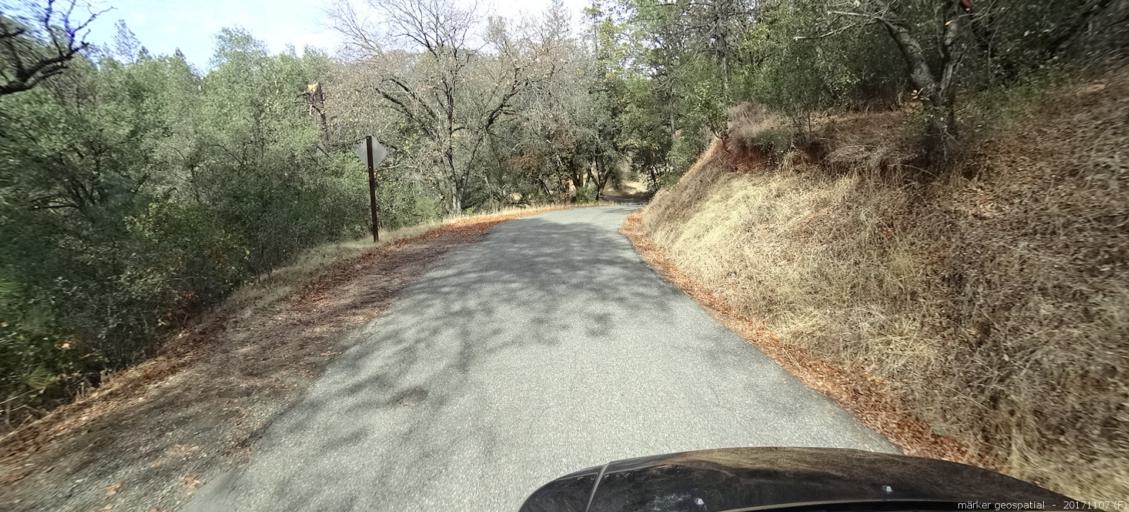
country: US
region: California
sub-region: Shasta County
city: Shasta
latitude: 40.5394
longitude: -122.5667
